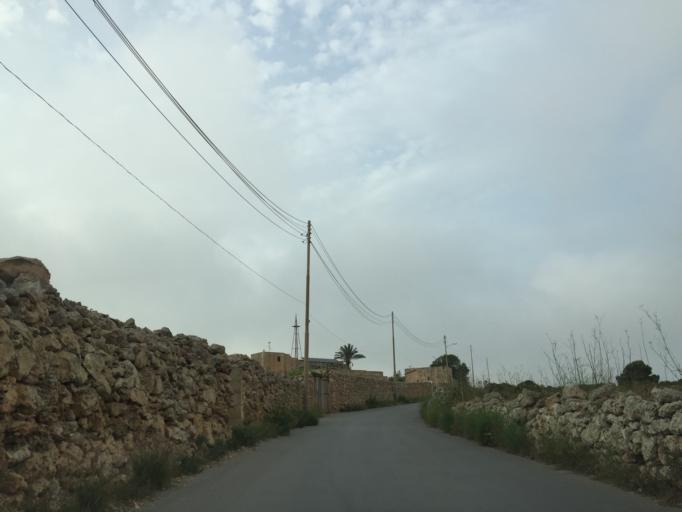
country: MT
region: L-Imgarr
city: Imgarr
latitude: 35.9346
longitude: 14.3895
